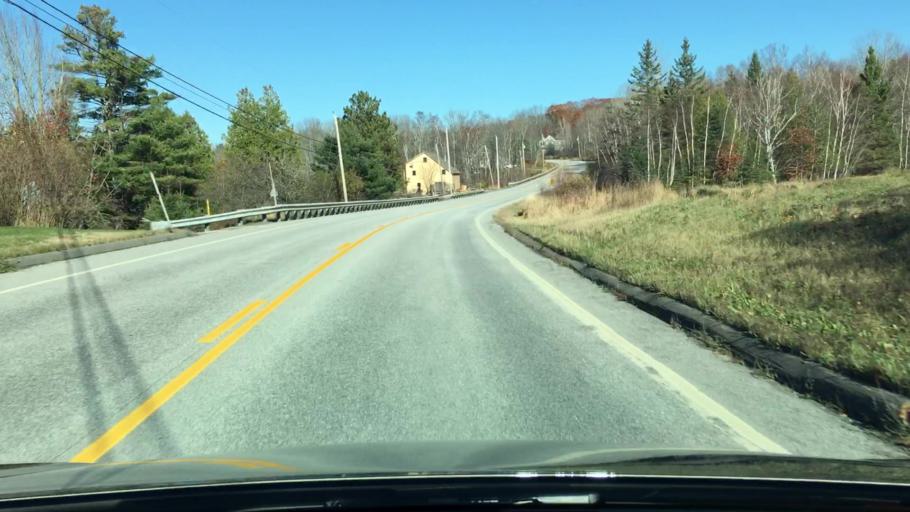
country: US
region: Maine
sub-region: Waldo County
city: Winterport
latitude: 44.6527
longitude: -68.8213
